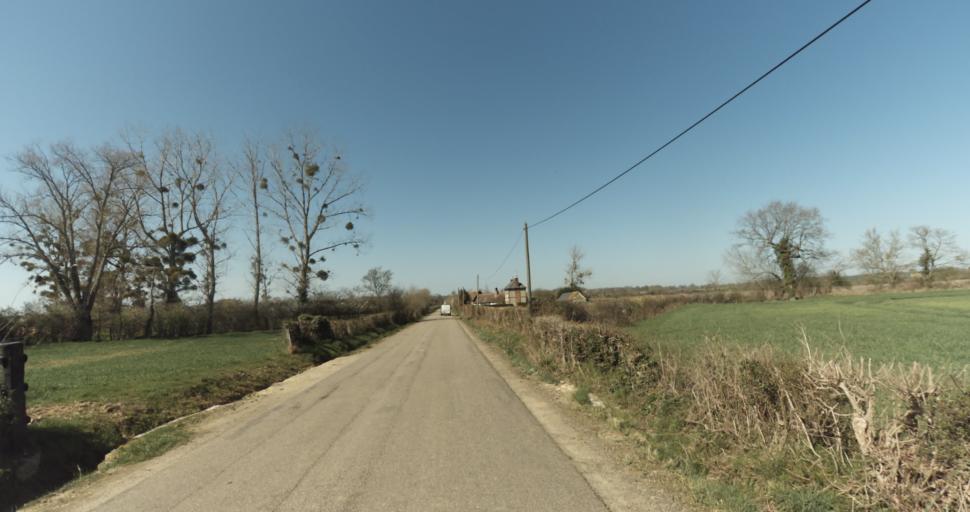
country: FR
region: Lower Normandy
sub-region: Departement du Calvados
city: Saint-Pierre-sur-Dives
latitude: 48.9935
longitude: 0.0184
